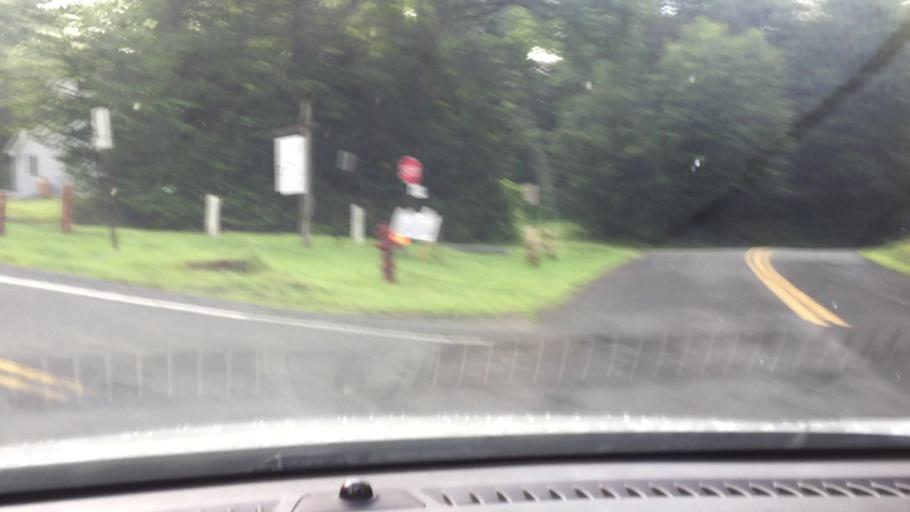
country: US
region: Massachusetts
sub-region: Hampshire County
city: Westhampton
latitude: 42.2405
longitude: -72.9041
